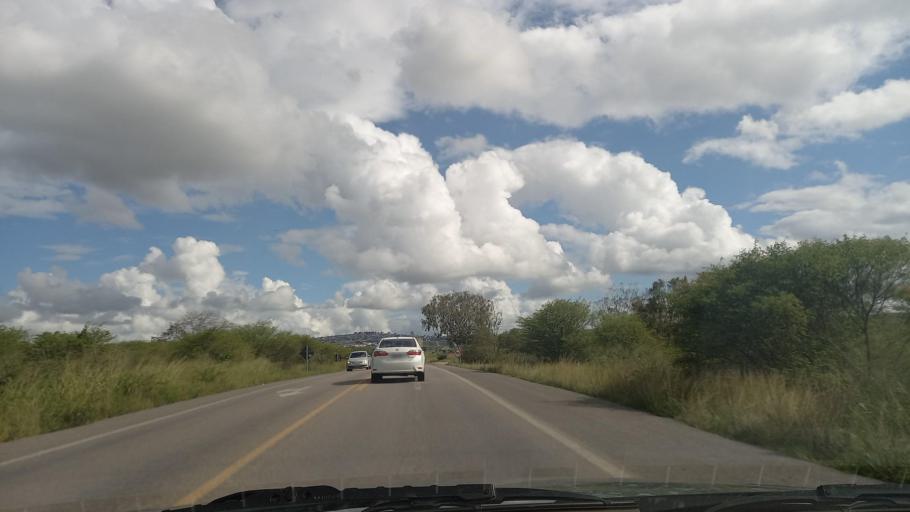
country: BR
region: Pernambuco
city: Garanhuns
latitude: -8.8341
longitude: -36.4546
